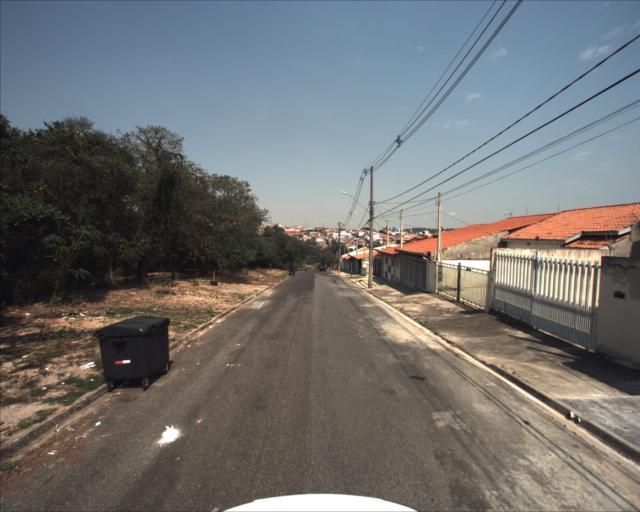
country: BR
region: Sao Paulo
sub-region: Sorocaba
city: Sorocaba
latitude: -23.4414
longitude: -47.4855
